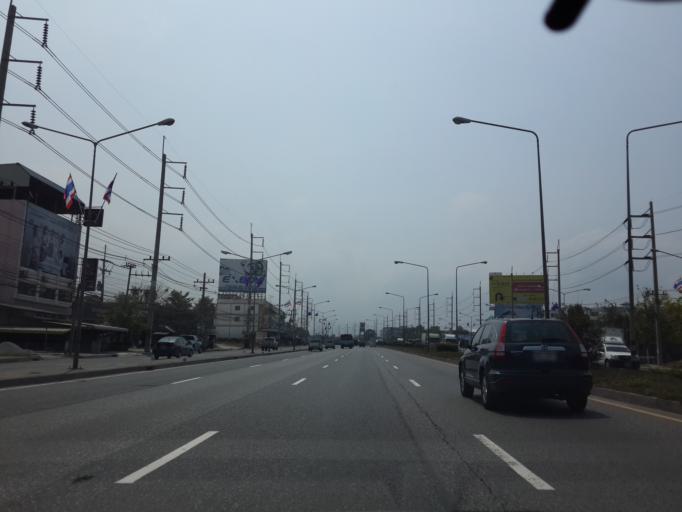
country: TH
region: Chon Buri
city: Chon Buri
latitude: 13.4082
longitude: 101.0011
